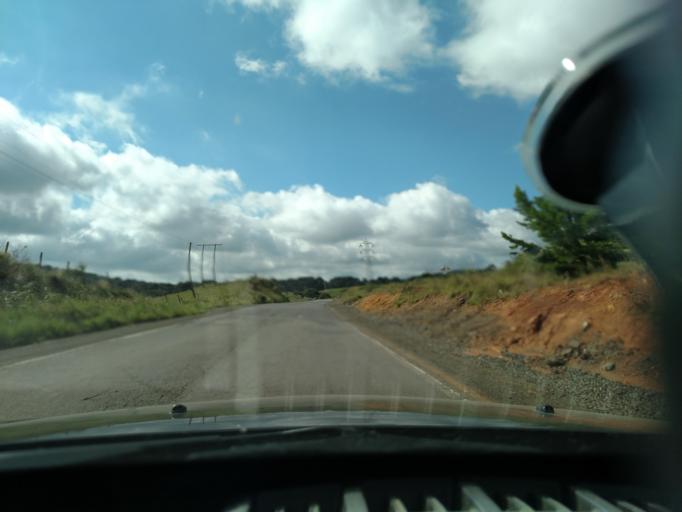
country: BR
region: Santa Catarina
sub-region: Lages
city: Lages
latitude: -27.8785
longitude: -50.1759
